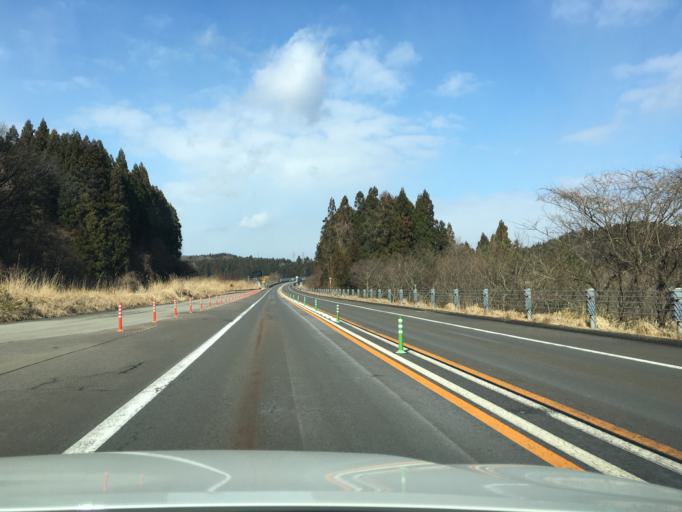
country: JP
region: Akita
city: Akita
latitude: 39.7528
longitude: 140.1441
